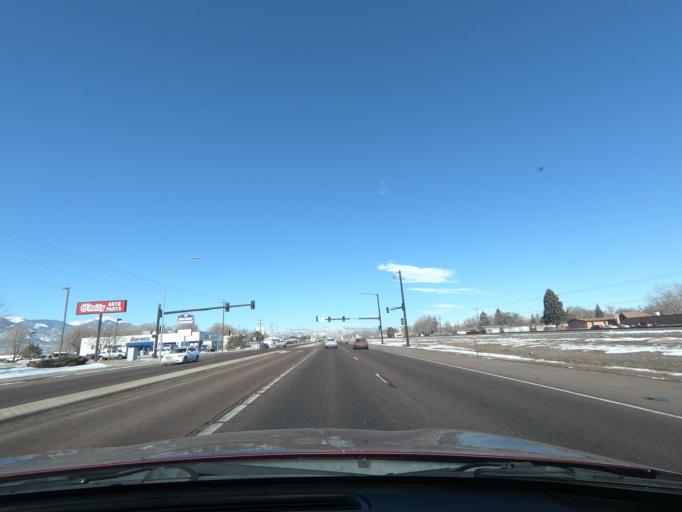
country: US
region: Colorado
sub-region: El Paso County
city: Security-Widefield
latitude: 38.7460
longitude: -104.7391
